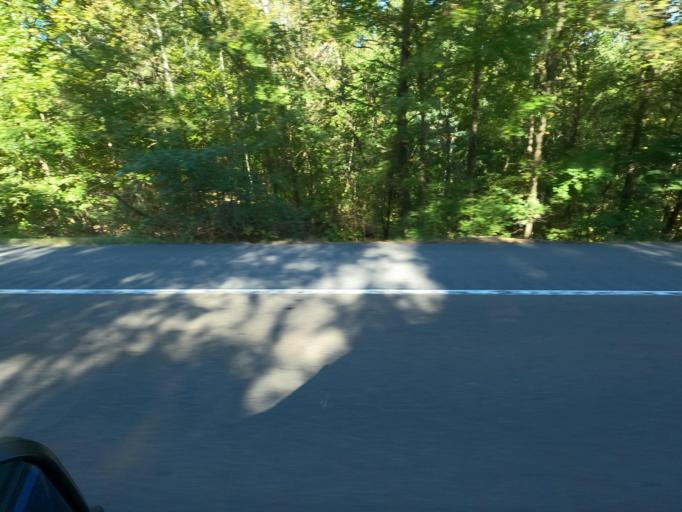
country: US
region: Tennessee
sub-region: Tipton County
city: Munford
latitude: 35.4336
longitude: -89.8042
